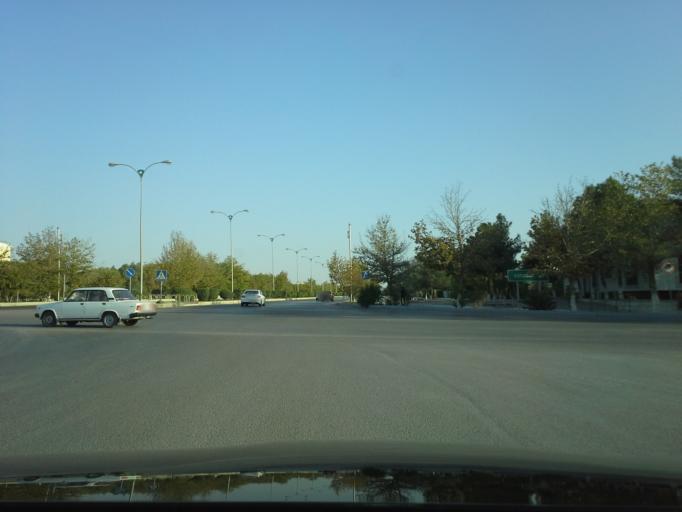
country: TM
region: Ahal
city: Abadan
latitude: 38.0349
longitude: 58.1885
